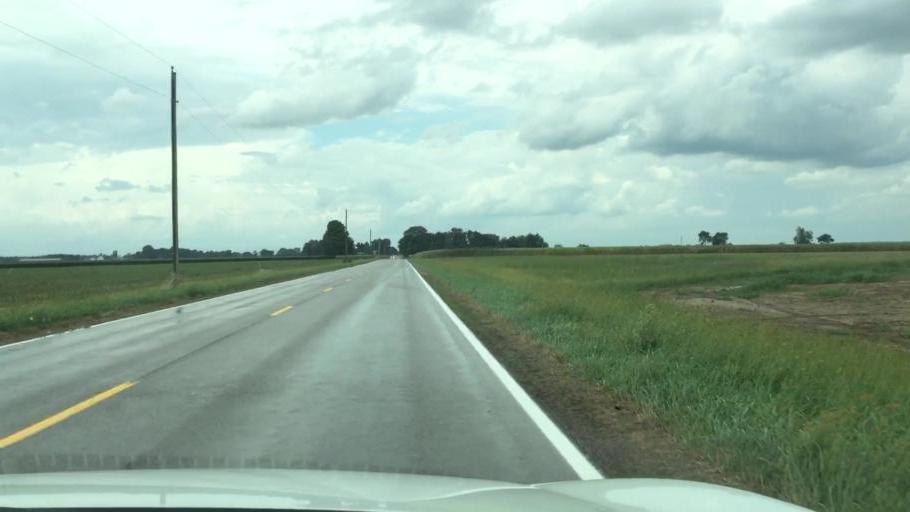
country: US
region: Ohio
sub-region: Champaign County
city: Urbana
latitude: 40.0410
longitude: -83.7101
